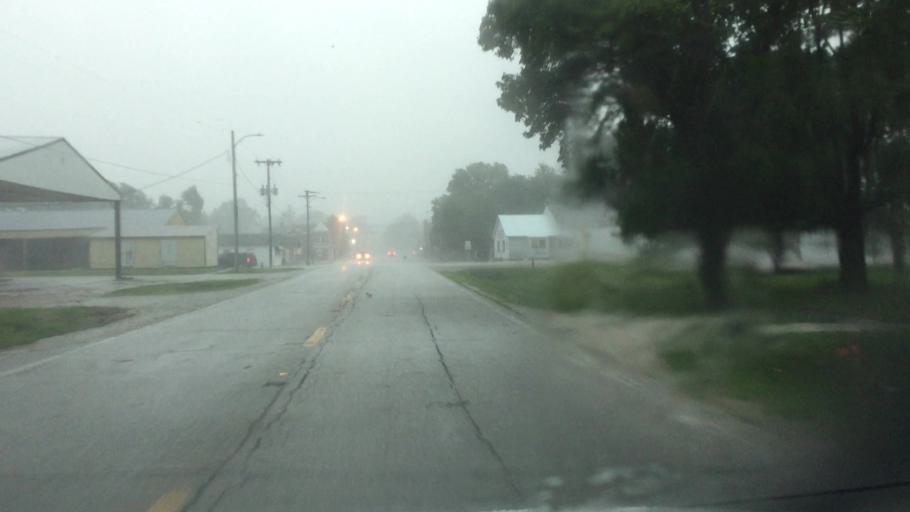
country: US
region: Illinois
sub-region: Adams County
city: Camp Point
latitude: 40.2315
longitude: -91.0611
